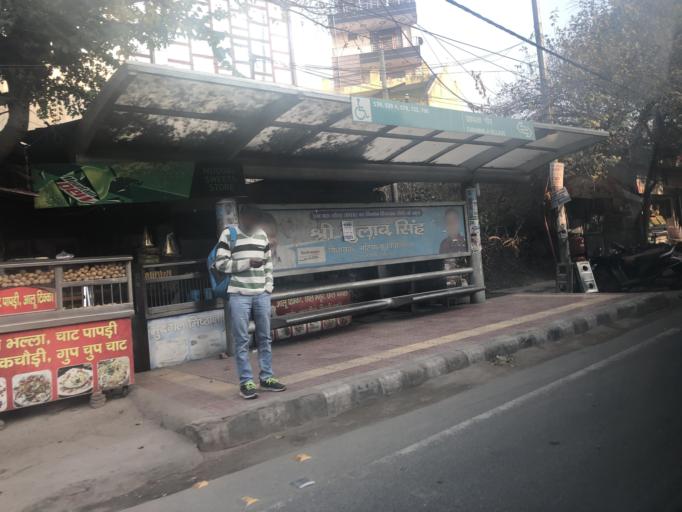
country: IN
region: Haryana
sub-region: Gurgaon
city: Gurgaon
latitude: 28.5614
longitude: 77.0021
